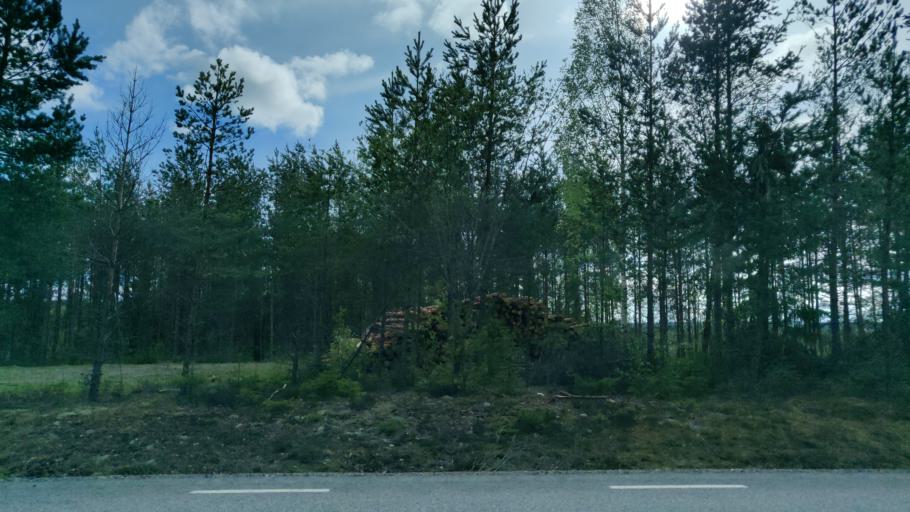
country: SE
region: Vaermland
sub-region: Forshaga Kommun
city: Deje
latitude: 59.5808
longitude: 13.4654
